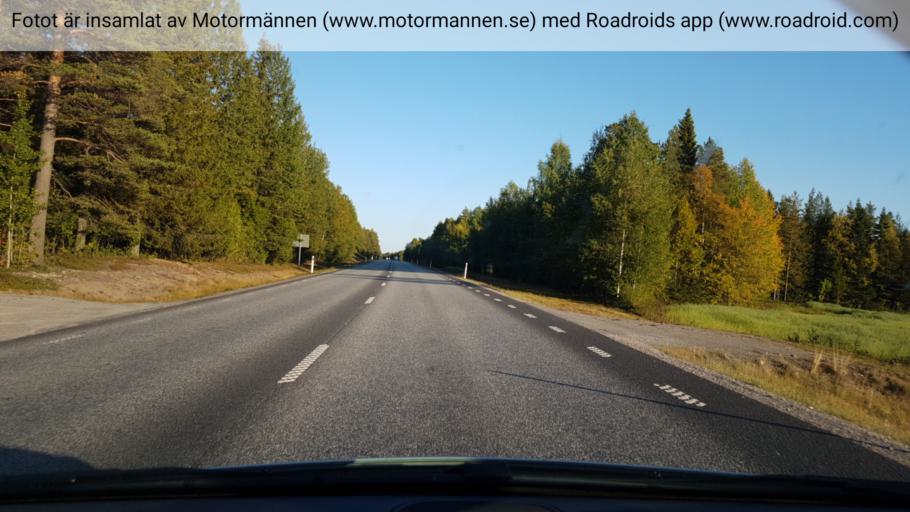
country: SE
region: Vaesterbotten
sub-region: Umea Kommun
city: Roback
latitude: 63.8540
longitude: 20.1011
